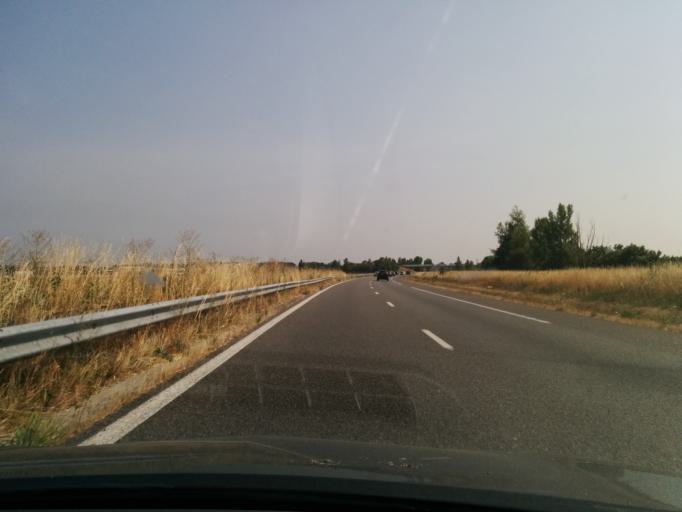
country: FR
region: Midi-Pyrenees
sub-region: Departement du Tarn
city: Coufouleux
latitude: 43.7875
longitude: 1.7410
